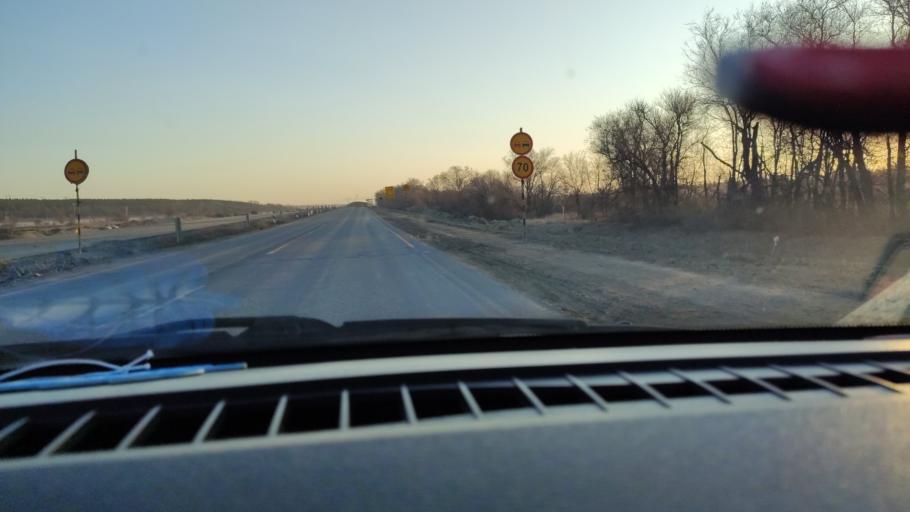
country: RU
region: Saratov
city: Sinodskoye
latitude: 52.0011
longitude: 46.6788
